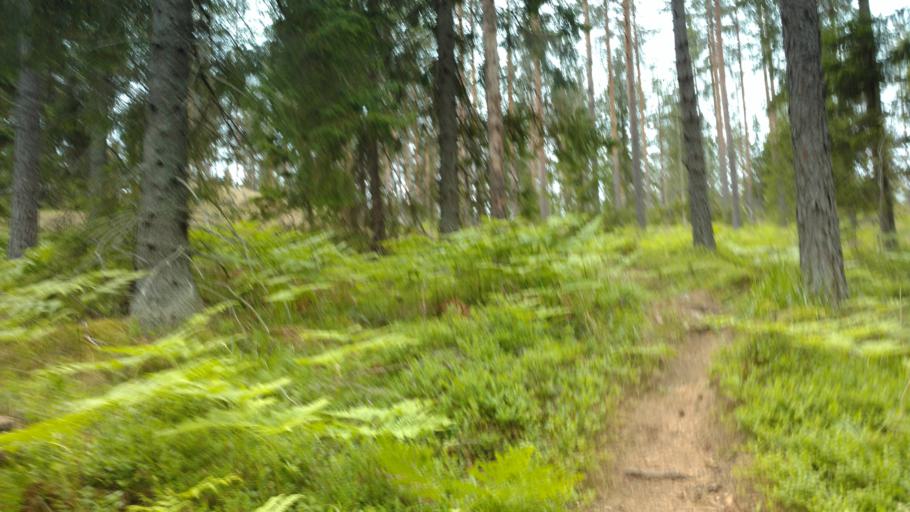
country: FI
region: Uusimaa
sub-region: Raaseporin
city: Pohja
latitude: 60.1170
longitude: 23.5586
